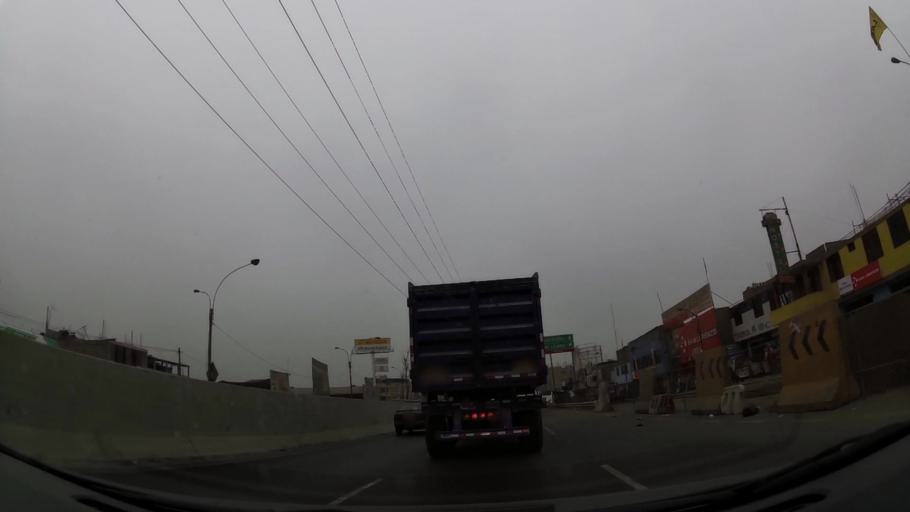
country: PE
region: Lima
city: Ventanilla
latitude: -11.8611
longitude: -77.0790
